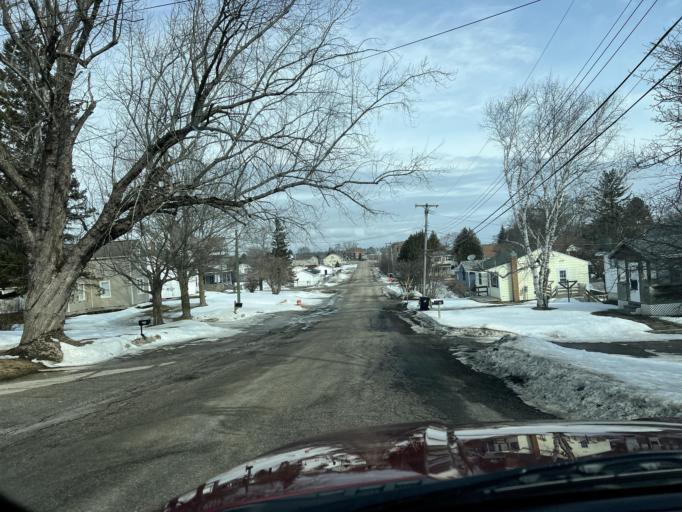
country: US
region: Michigan
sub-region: Mackinac County
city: Saint Ignace
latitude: 45.8633
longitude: -84.7241
